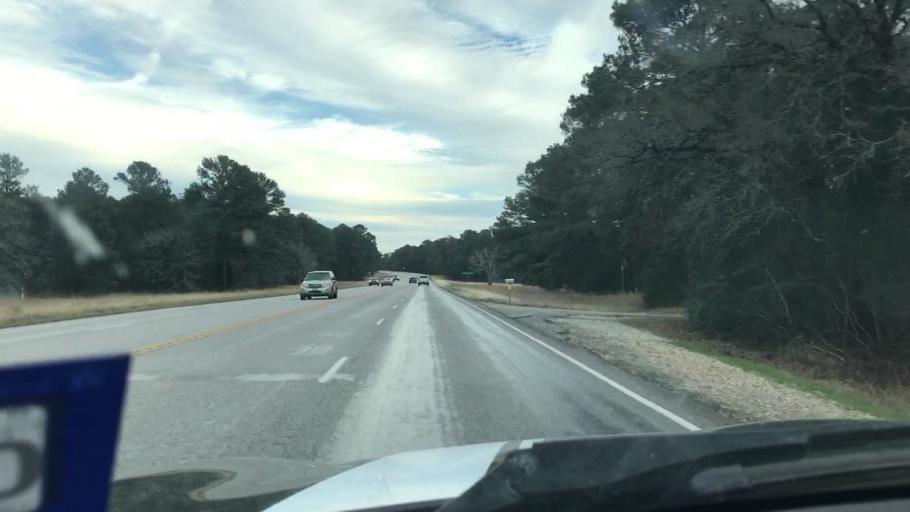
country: US
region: Texas
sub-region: Bastrop County
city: Camp Swift
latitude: 30.2441
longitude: -97.2175
